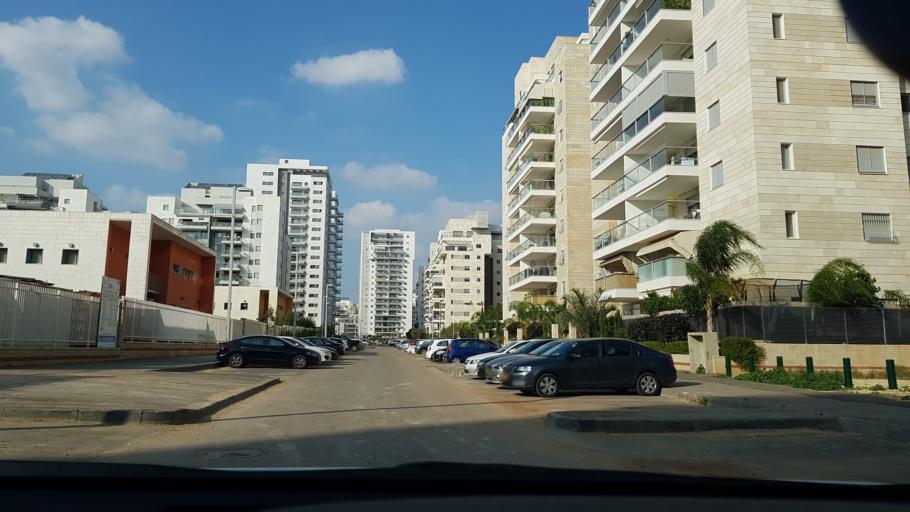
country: IL
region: Central District
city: Ness Ziona
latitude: 31.9003
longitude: 34.8235
